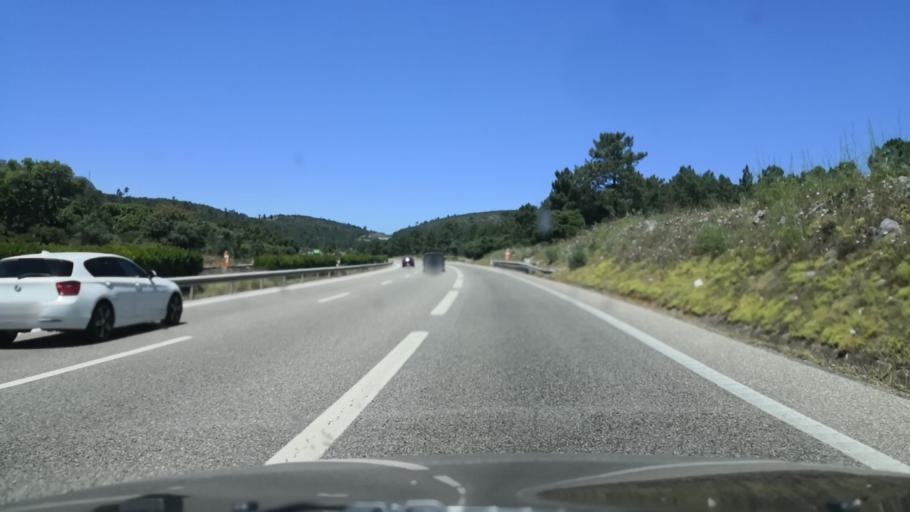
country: PT
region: Santarem
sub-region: Alcanena
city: Alcanena
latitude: 39.4983
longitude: -8.6537
